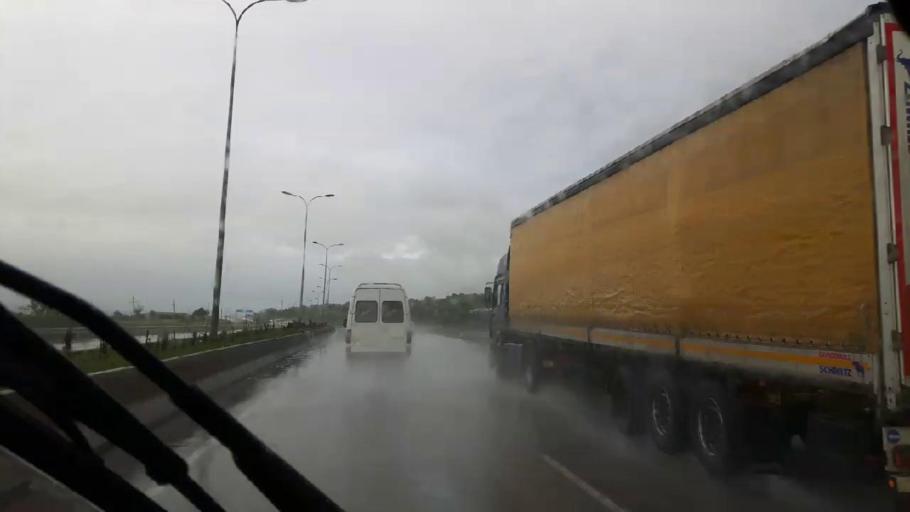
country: GE
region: Shida Kartli
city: Gori
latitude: 42.0269
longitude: 44.1894
